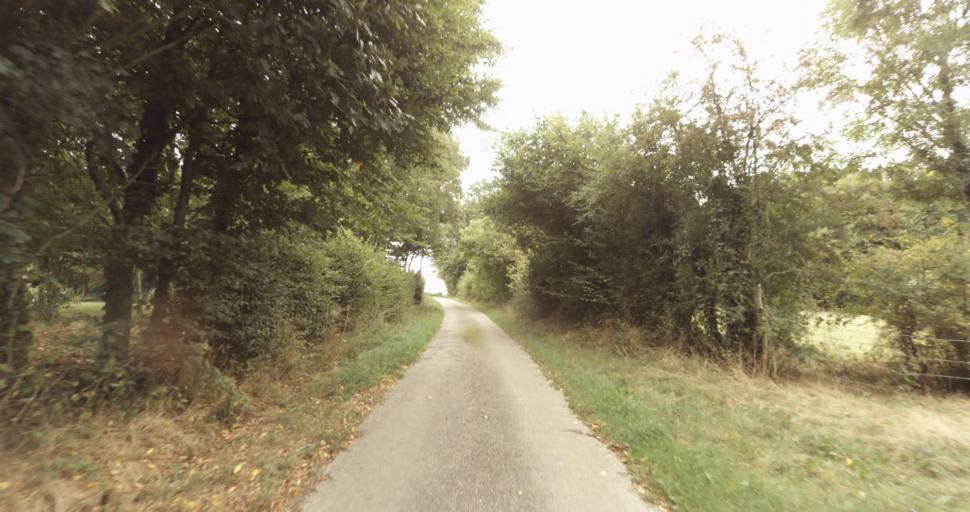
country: FR
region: Lower Normandy
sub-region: Departement du Calvados
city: Orbec
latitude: 48.9167
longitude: 0.3556
